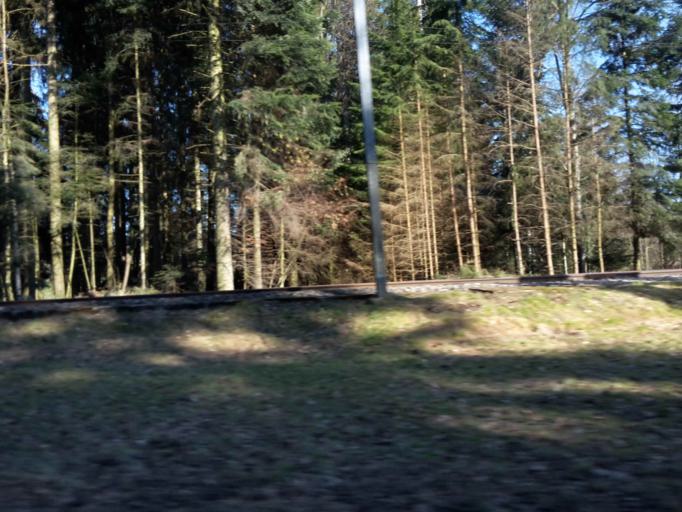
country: CH
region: Bern
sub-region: Emmental District
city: Sumiswald
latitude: 47.0637
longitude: 7.7492
